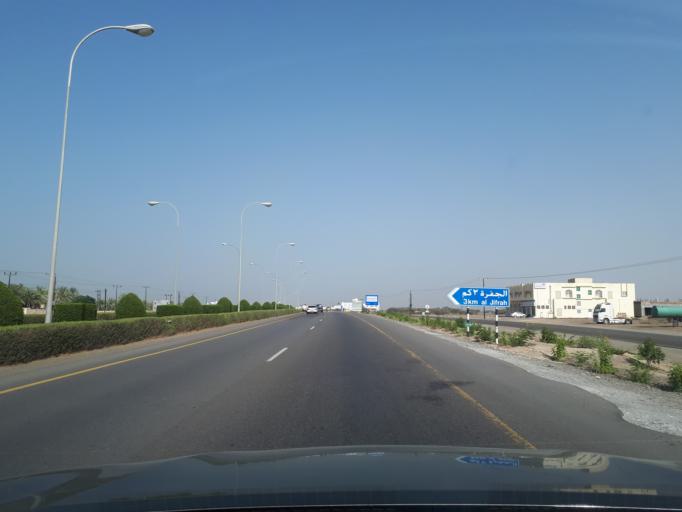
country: OM
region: Al Batinah
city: Al Sohar
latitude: 24.4133
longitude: 56.6330
